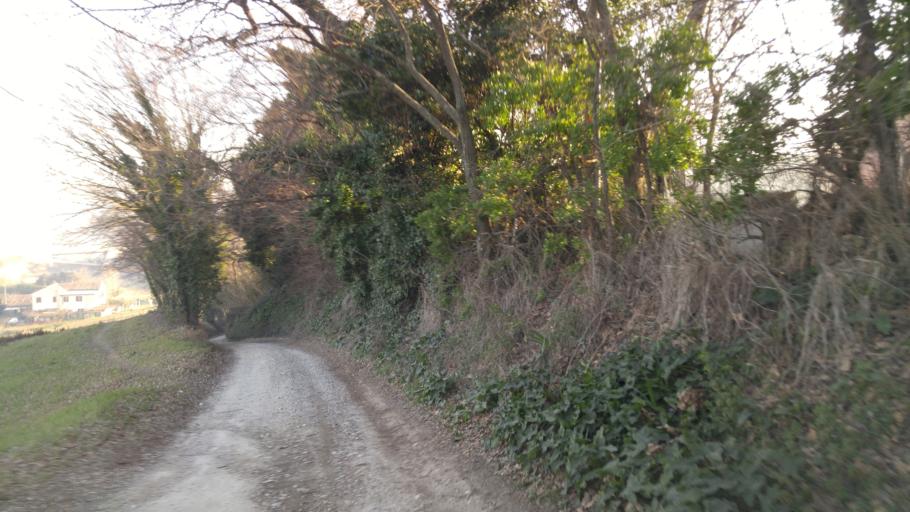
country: IT
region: The Marches
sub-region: Provincia di Pesaro e Urbino
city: Fenile
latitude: 43.8492
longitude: 12.9653
